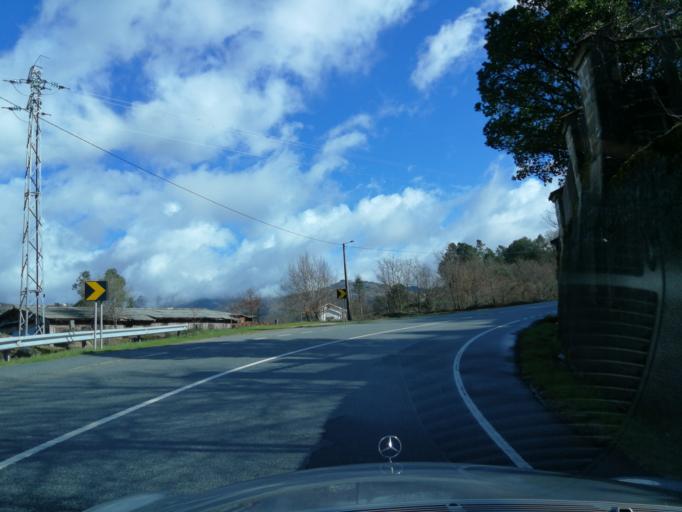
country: ES
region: Galicia
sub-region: Provincia de Ourense
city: Entrimo
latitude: 41.8649
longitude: -8.2128
